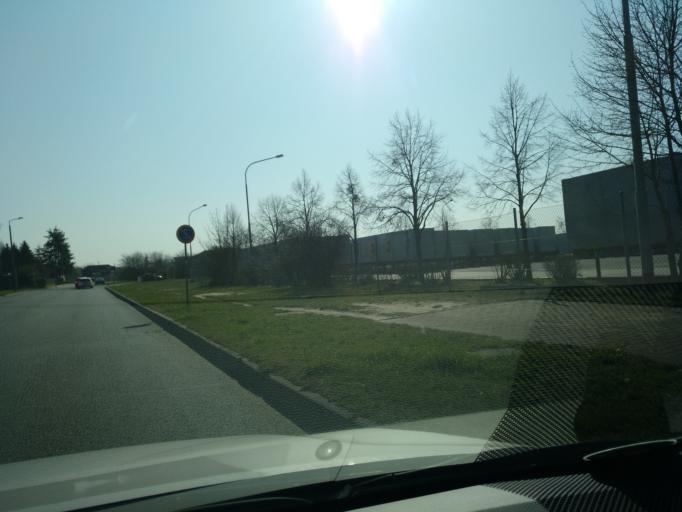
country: DE
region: Brandenburg
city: Hoppegarten
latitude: 52.5067
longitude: 13.6449
